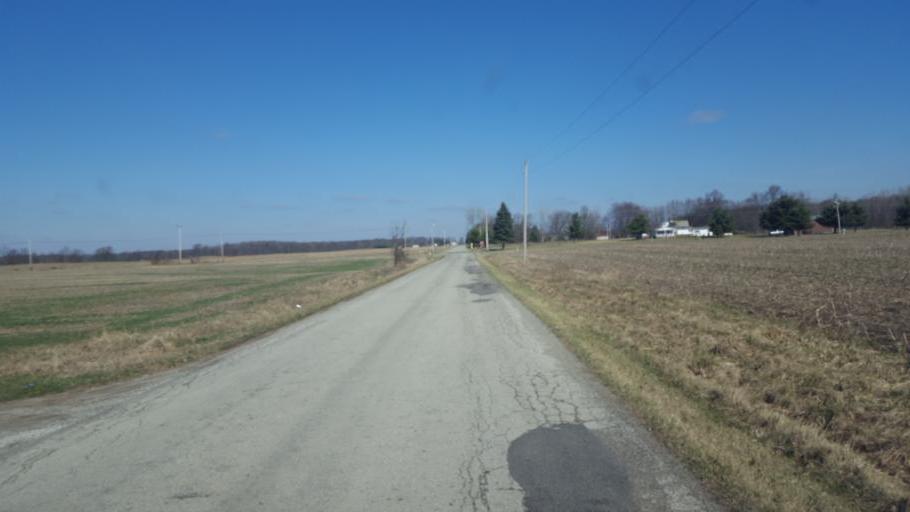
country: US
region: Ohio
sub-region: Morrow County
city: Mount Gilead
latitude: 40.5139
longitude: -82.7929
